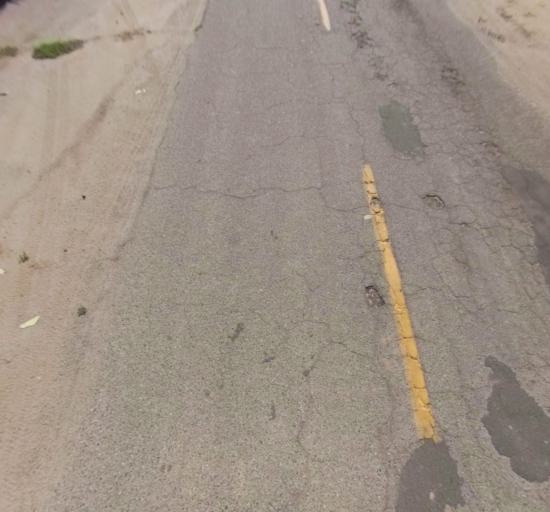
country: US
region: California
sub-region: Madera County
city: Madera
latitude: 36.9456
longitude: -120.1142
